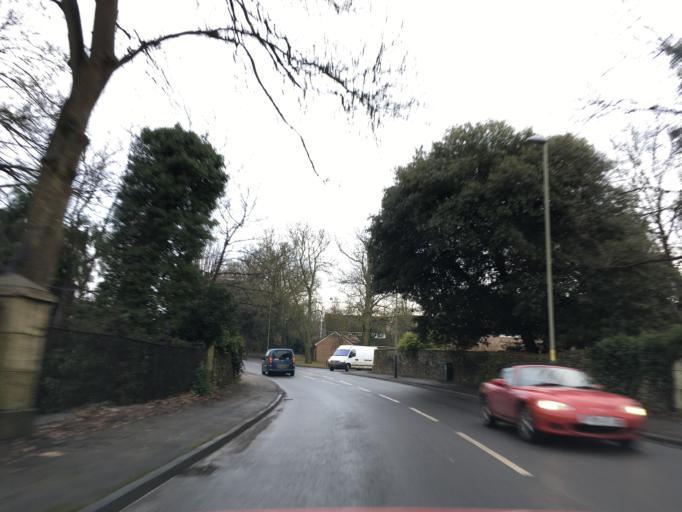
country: GB
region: England
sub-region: Gloucestershire
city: Charlton Kings
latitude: 51.8878
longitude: -2.0578
